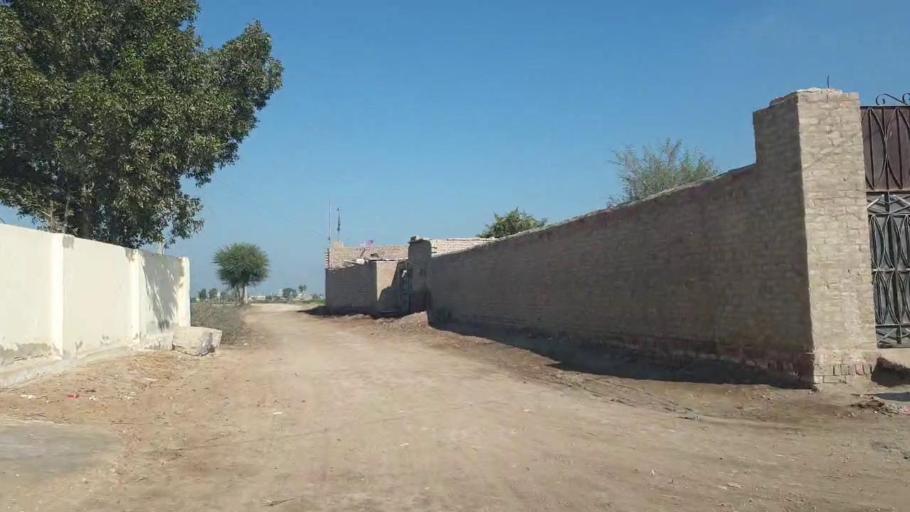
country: PK
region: Sindh
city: Bhit Shah
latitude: 25.8867
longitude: 68.5266
